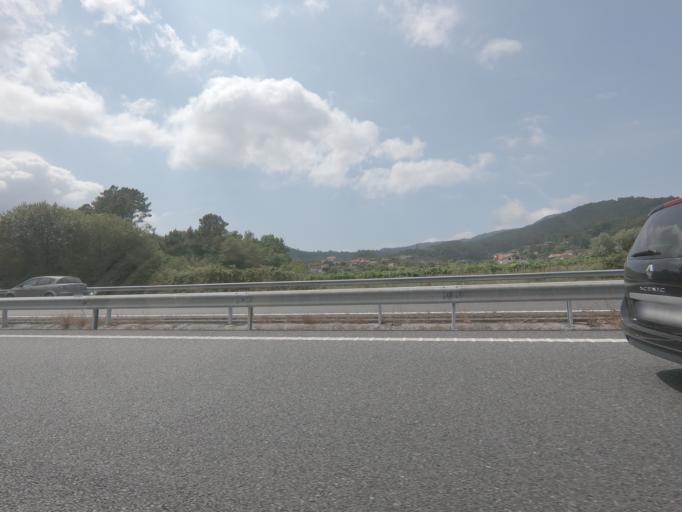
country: ES
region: Galicia
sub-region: Provincia de Pontevedra
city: Tui
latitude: 42.0570
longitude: -8.6538
